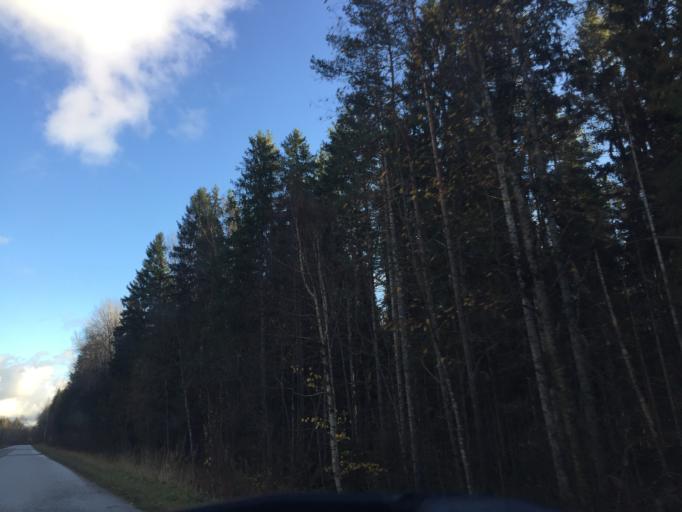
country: LV
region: Incukalns
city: Incukalns
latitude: 57.0874
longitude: 24.7701
